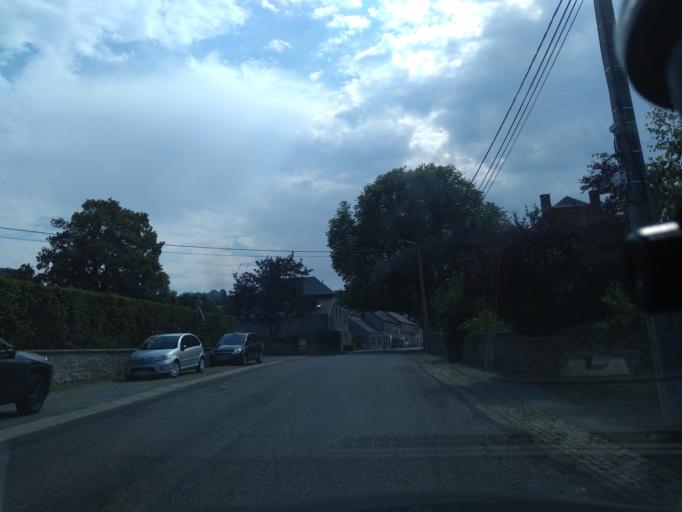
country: BE
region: Wallonia
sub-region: Province de Namur
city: Dinant
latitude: 50.2065
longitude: 4.8970
